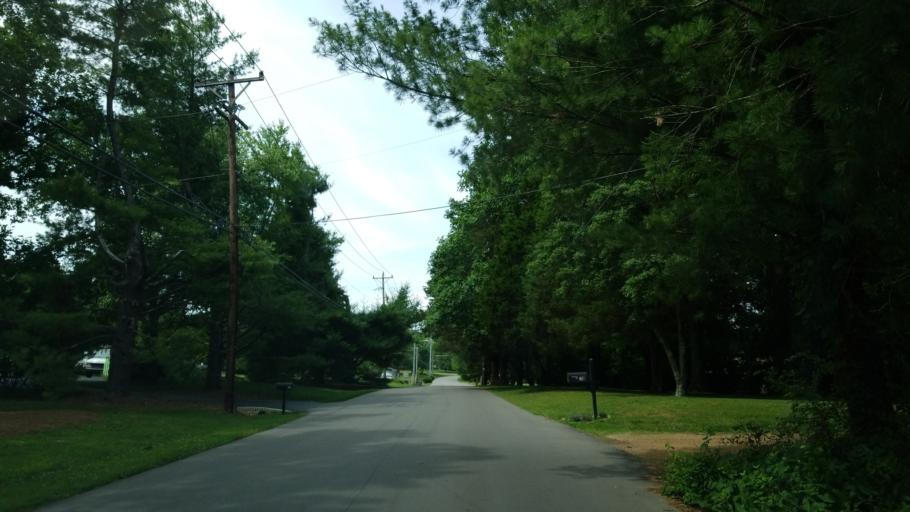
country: US
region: Tennessee
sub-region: Williamson County
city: Brentwood
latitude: 36.0352
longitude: -86.8219
